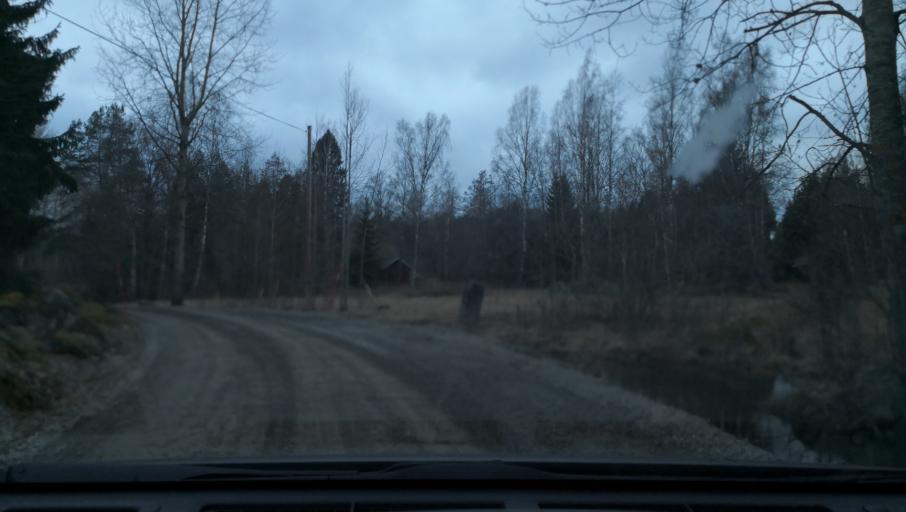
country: SE
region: Vaestmanland
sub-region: Kopings Kommun
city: Kolsva
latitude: 59.5649
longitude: 15.7850
